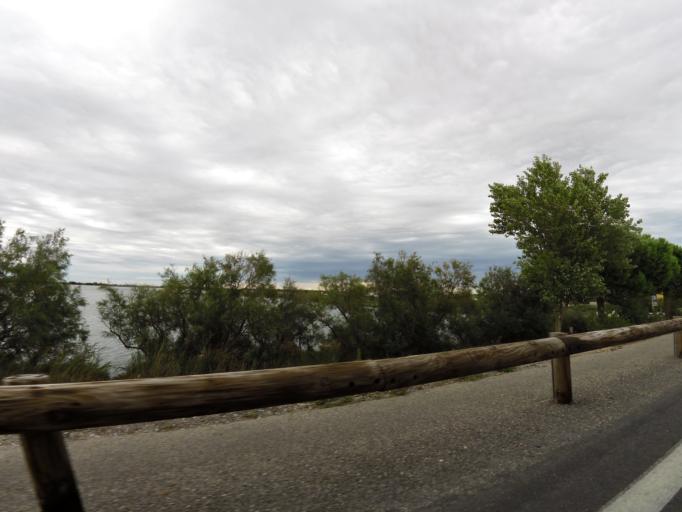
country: FR
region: Languedoc-Roussillon
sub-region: Departement du Gard
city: Le Grau-du-Roi
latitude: 43.5410
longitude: 4.1423
